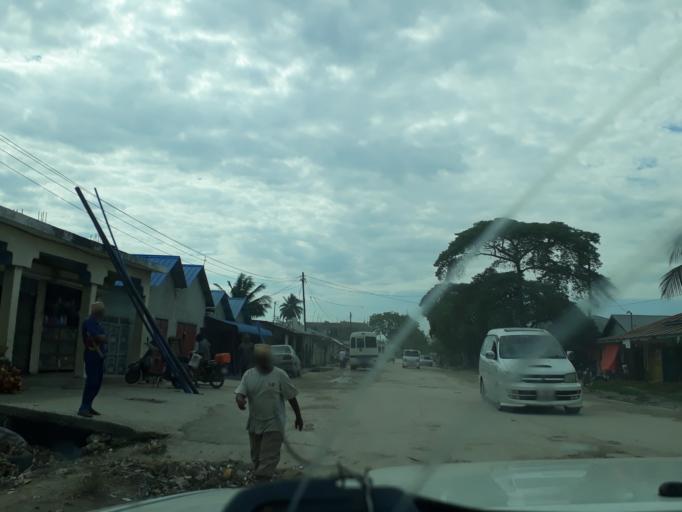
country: TZ
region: Zanzibar Central/South
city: Koani
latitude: -6.0828
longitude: 39.2226
